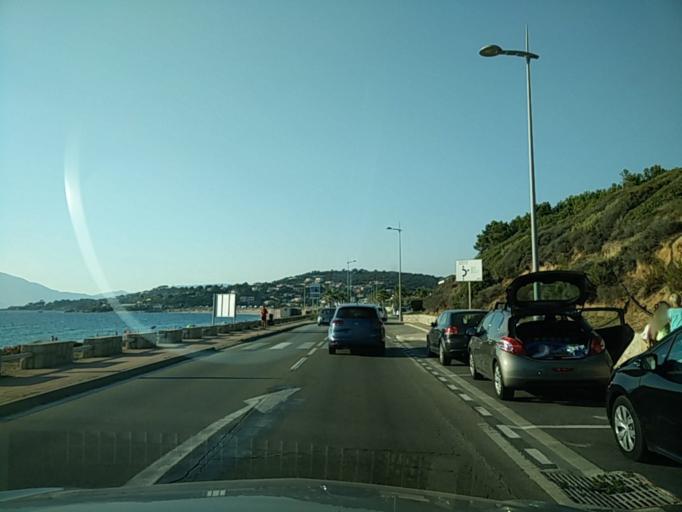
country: FR
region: Corsica
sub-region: Departement de la Corse-du-Sud
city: Pietrosella
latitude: 41.8625
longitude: 8.7913
